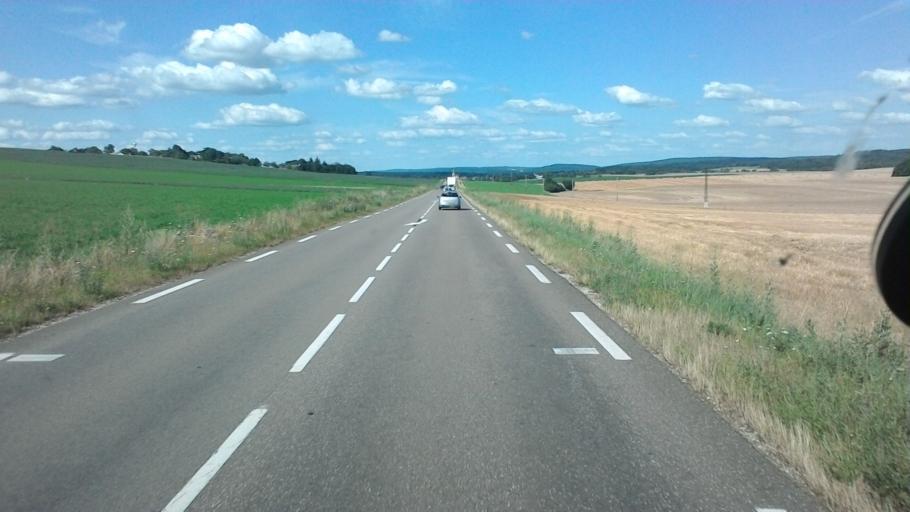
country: FR
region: Franche-Comte
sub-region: Departement de la Haute-Saone
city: Gy
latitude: 47.4708
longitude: 5.9232
